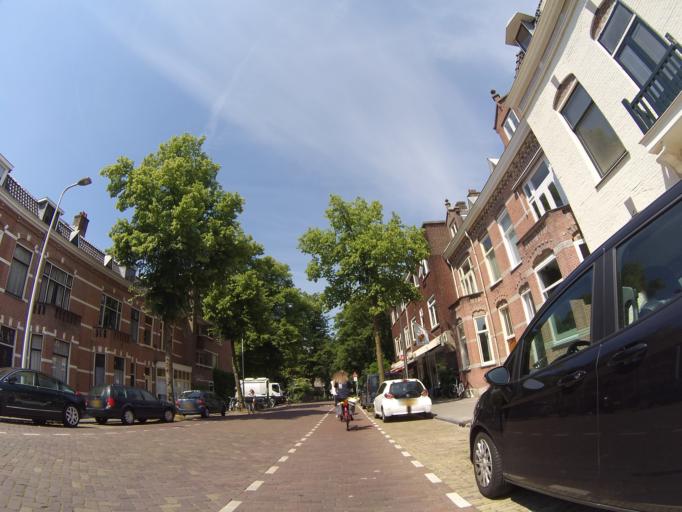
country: NL
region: Utrecht
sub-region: Gemeente Utrecht
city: Utrecht
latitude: 52.0868
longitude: 5.1429
